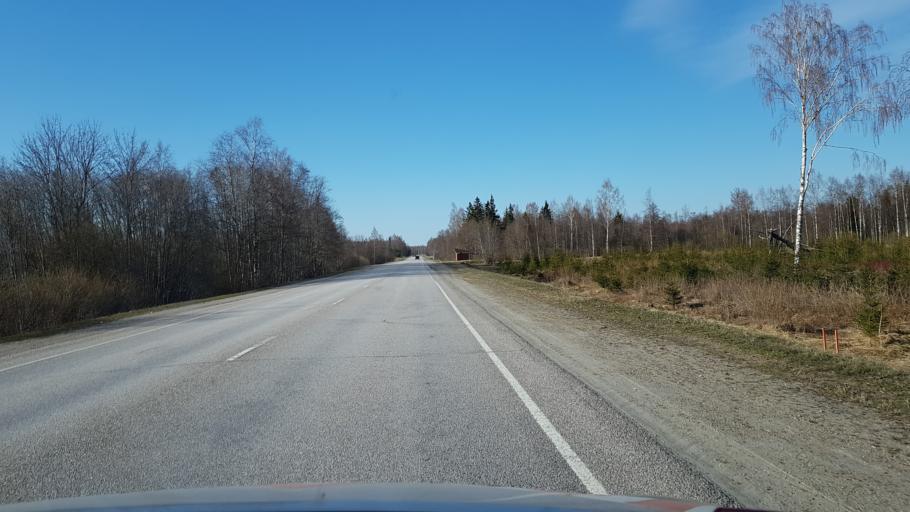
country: EE
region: Ida-Virumaa
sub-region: Johvi vald
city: Johvi
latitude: 59.1727
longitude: 27.3507
